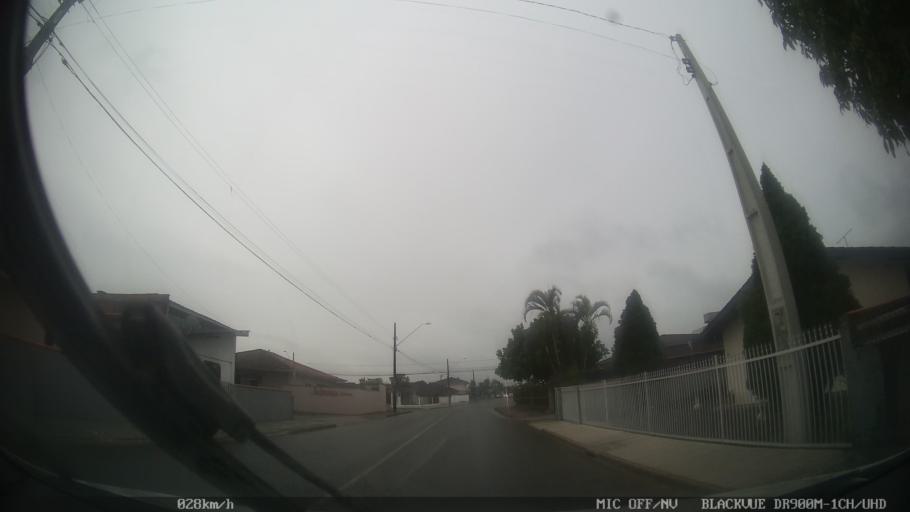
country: BR
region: Santa Catarina
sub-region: Joinville
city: Joinville
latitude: -26.2357
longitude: -48.8125
